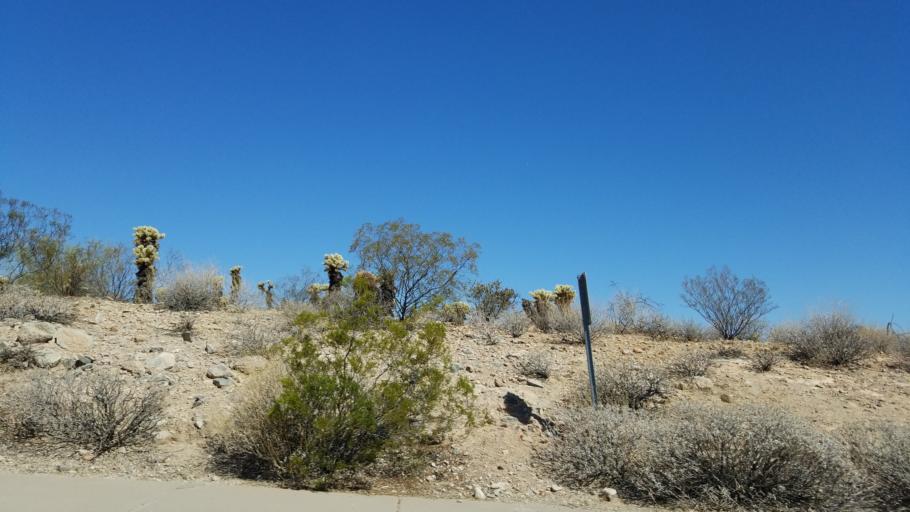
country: US
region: Arizona
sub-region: Maricopa County
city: Fountain Hills
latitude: 33.6081
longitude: -111.7464
